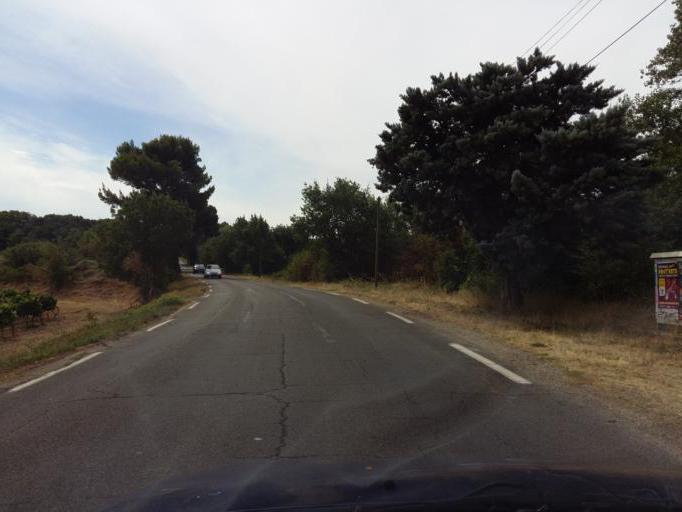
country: FR
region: Provence-Alpes-Cote d'Azur
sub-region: Departement du Vaucluse
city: Saint-Didier
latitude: 44.0144
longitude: 5.1027
